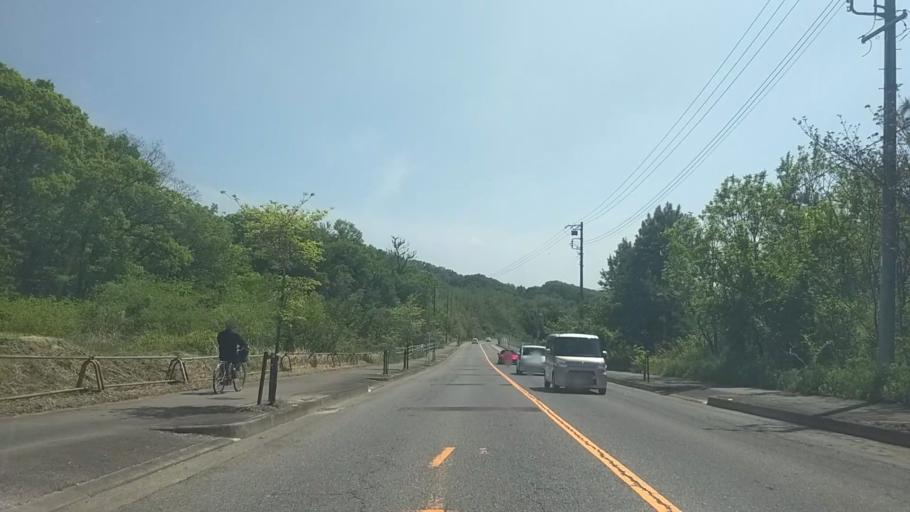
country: JP
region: Aichi
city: Okazaki
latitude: 34.9749
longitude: 137.1973
